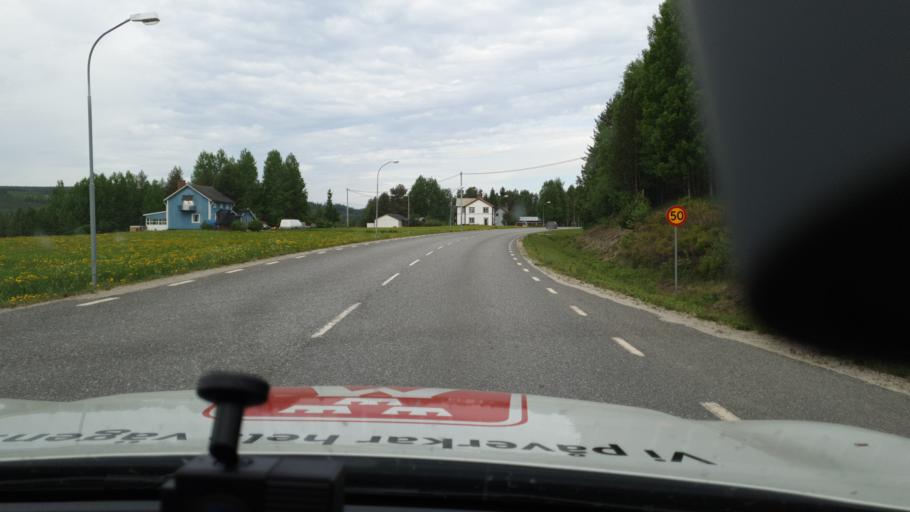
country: SE
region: Vaesterbotten
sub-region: Mala Kommun
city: Mala
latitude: 64.9874
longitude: 18.5113
